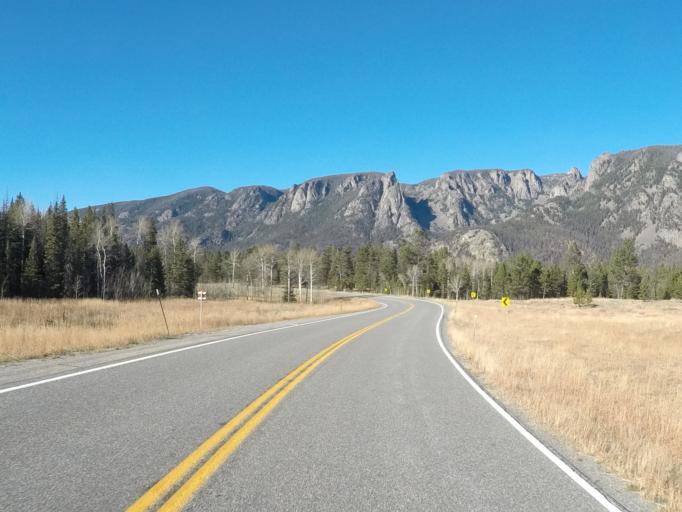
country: US
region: Montana
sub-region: Carbon County
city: Red Lodge
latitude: 44.8484
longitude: -109.5017
